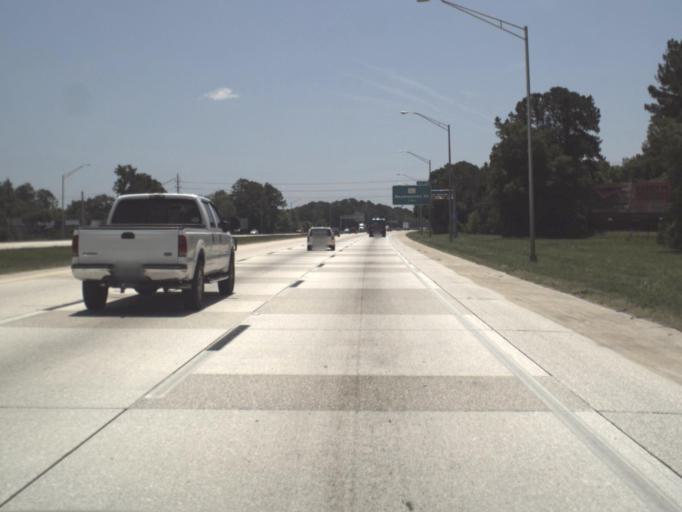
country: US
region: Florida
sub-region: Duval County
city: Jacksonville
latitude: 30.2376
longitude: -81.5827
